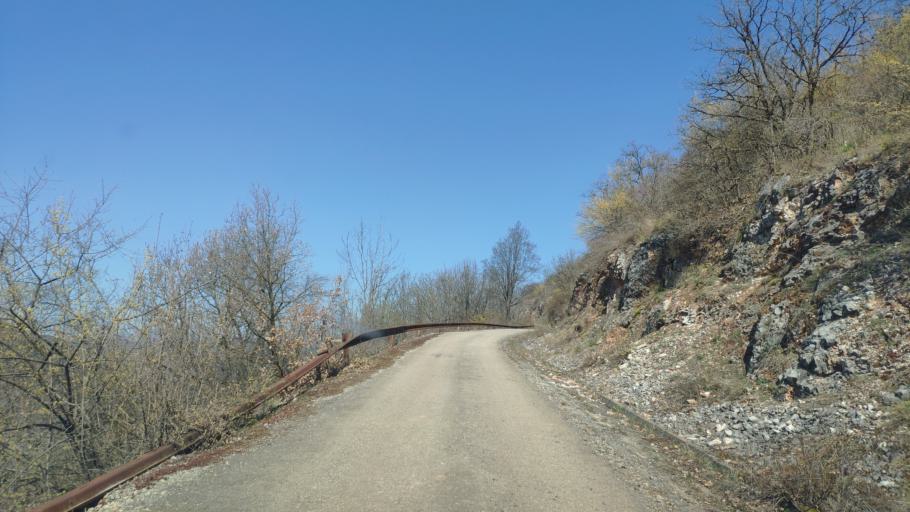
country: SK
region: Kosicky
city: Roznava
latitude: 48.5772
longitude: 20.4054
